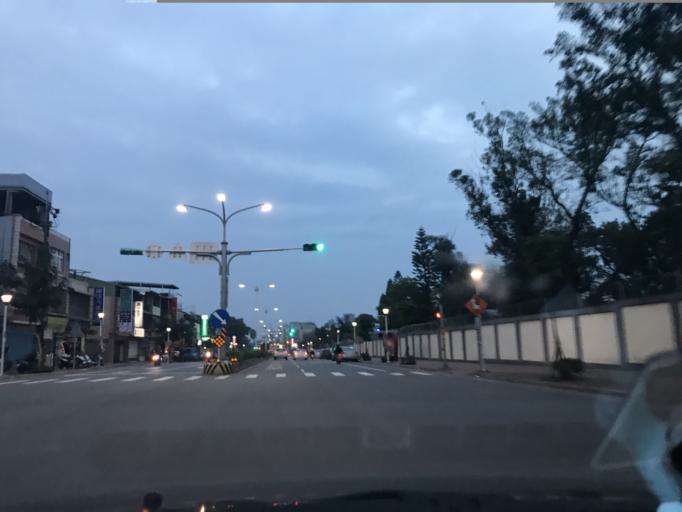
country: TW
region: Taiwan
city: Daxi
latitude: 24.9309
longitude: 121.2391
